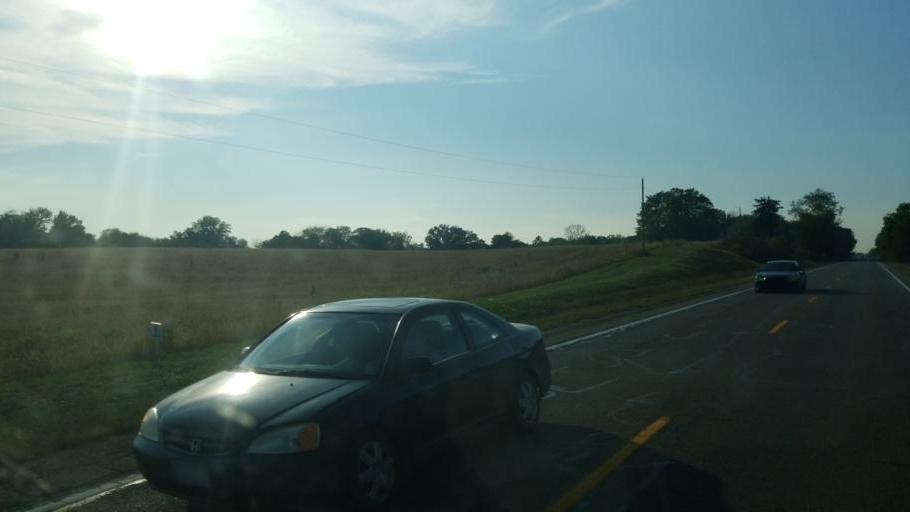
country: US
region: Ohio
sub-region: Morrow County
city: Mount Gilead
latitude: 40.4847
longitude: -82.6943
